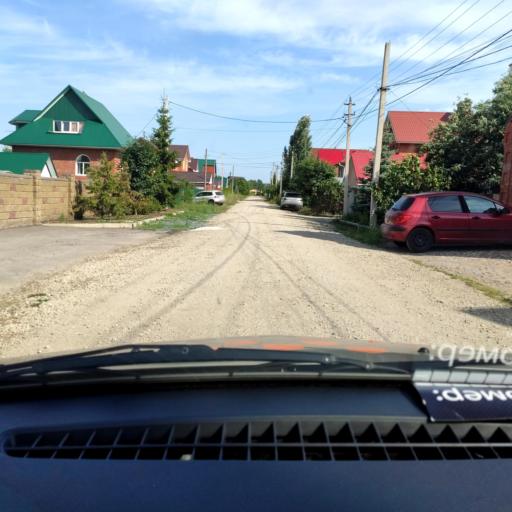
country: RU
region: Bashkortostan
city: Ufa
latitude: 54.6239
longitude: 55.9195
